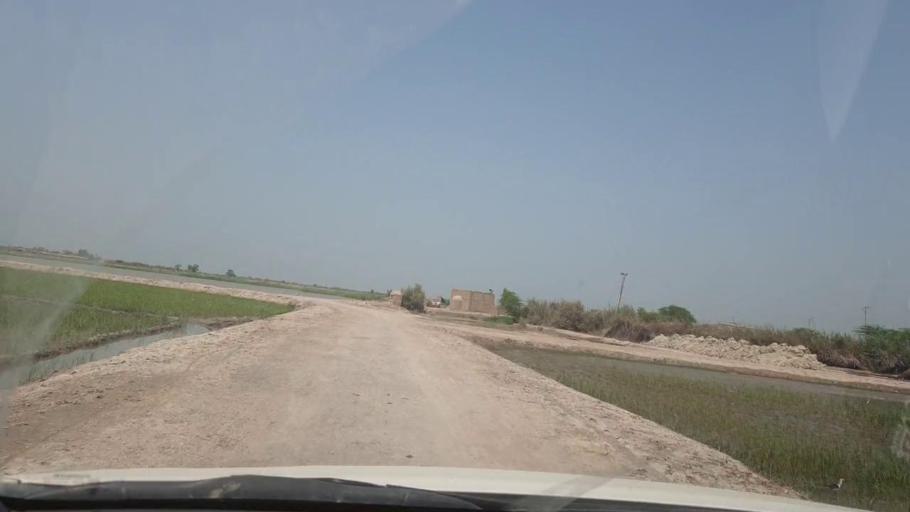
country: PK
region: Sindh
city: Lakhi
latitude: 27.8758
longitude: 68.7355
